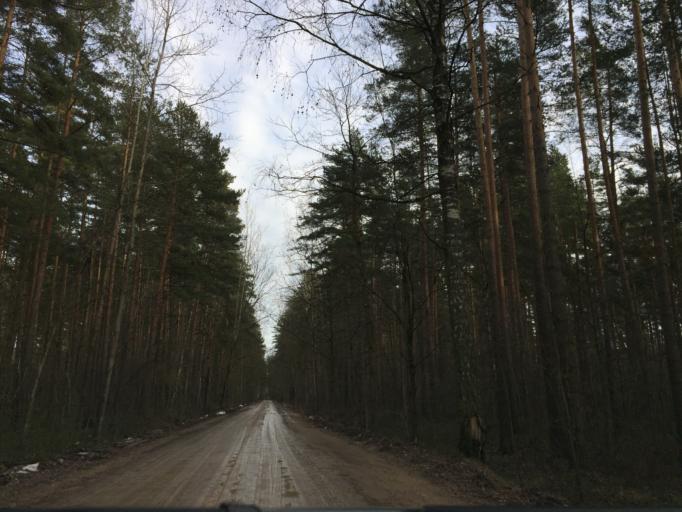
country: LV
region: Stopini
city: Ulbroka
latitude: 56.9221
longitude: 24.2942
